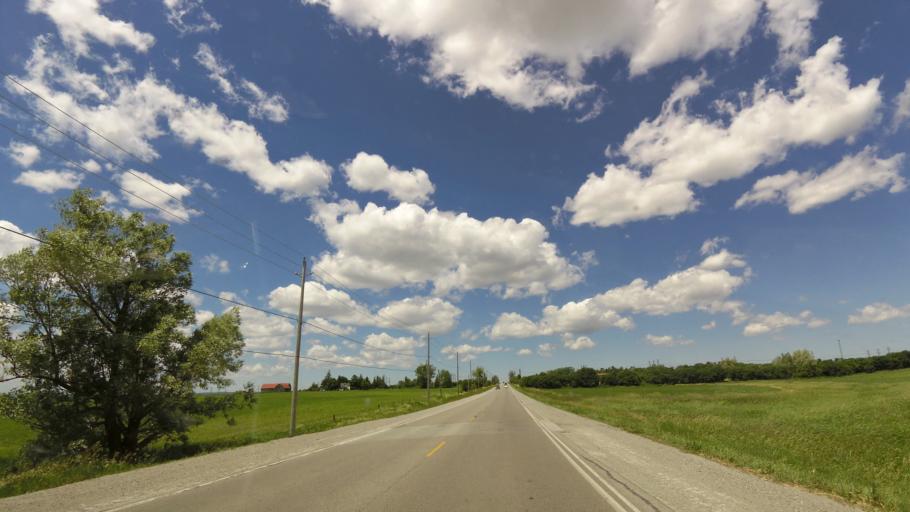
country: CA
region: Ontario
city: Oshawa
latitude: 43.9652
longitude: -78.8608
